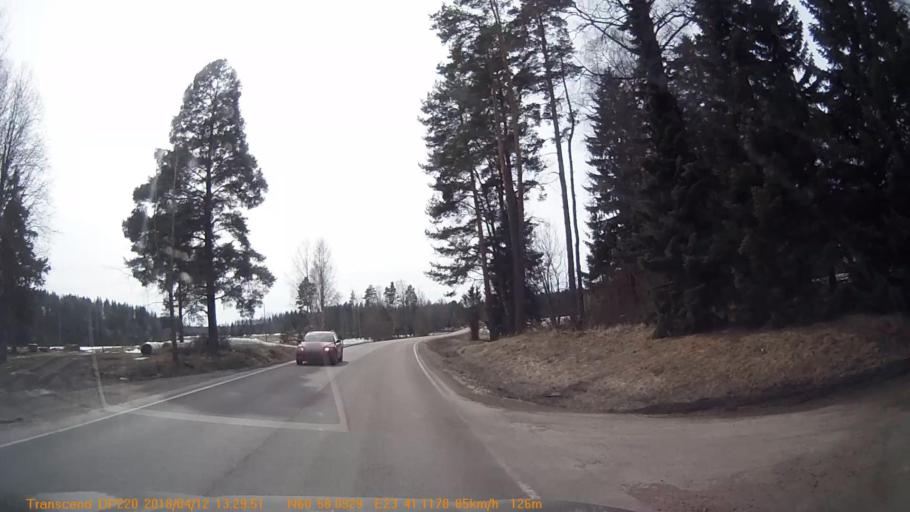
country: FI
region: Haeme
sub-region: Forssa
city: Forssa
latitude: 60.9680
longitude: 23.6849
